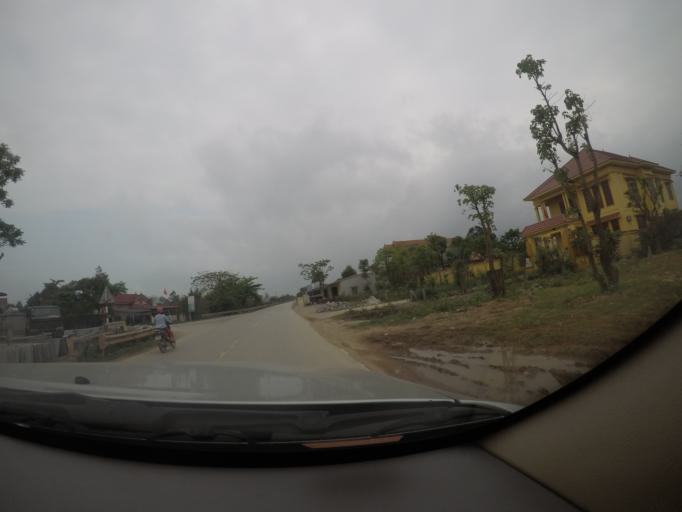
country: VN
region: Quang Binh
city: Kien Giang
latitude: 17.2350
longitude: 106.6949
